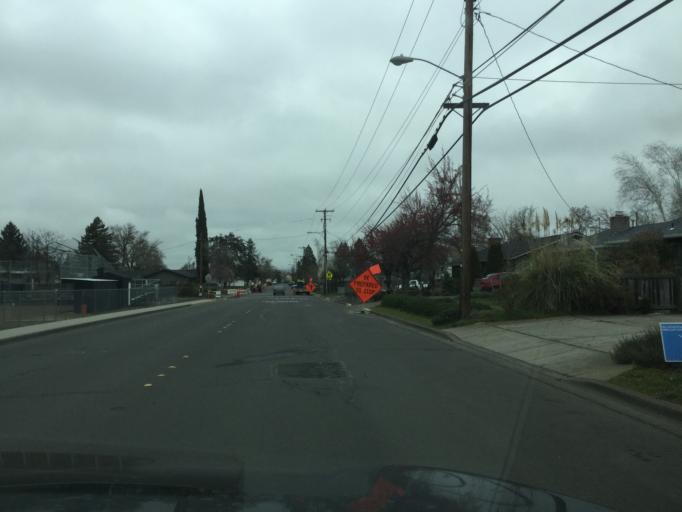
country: US
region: Oregon
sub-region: Jackson County
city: Central Point
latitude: 42.3811
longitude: -122.9196
